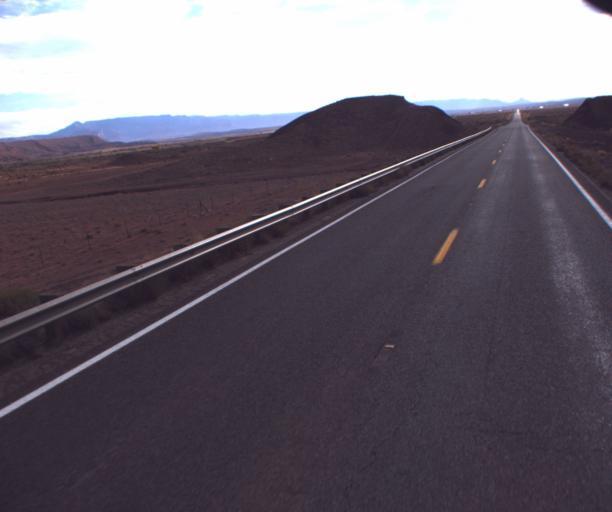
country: US
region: Arizona
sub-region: Apache County
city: Many Farms
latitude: 36.5386
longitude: -109.5197
